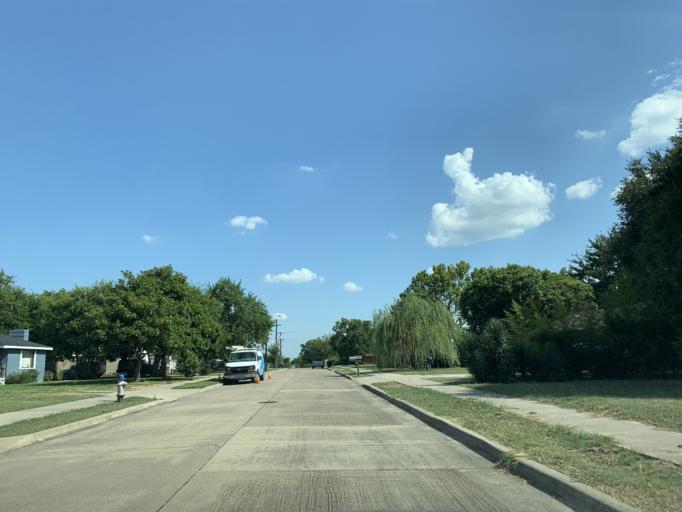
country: US
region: Texas
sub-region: Dallas County
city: Hutchins
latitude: 32.6552
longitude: -96.7766
